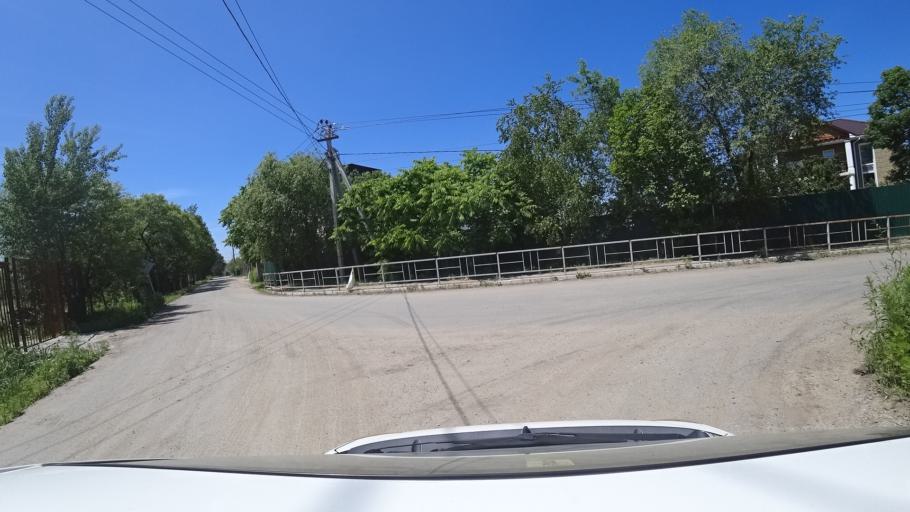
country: RU
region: Khabarovsk Krai
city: Topolevo
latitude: 48.5103
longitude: 135.1773
